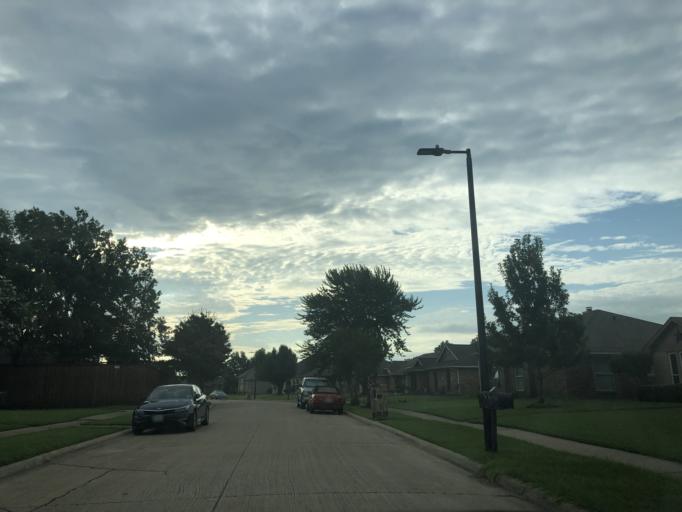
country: US
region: Texas
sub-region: Dallas County
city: Sunnyvale
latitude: 32.8423
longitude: -96.5633
